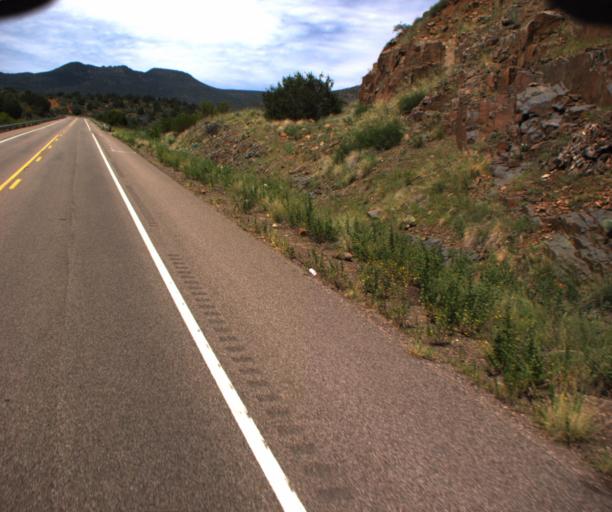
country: US
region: Arizona
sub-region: Gila County
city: Globe
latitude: 33.5510
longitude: -110.6848
